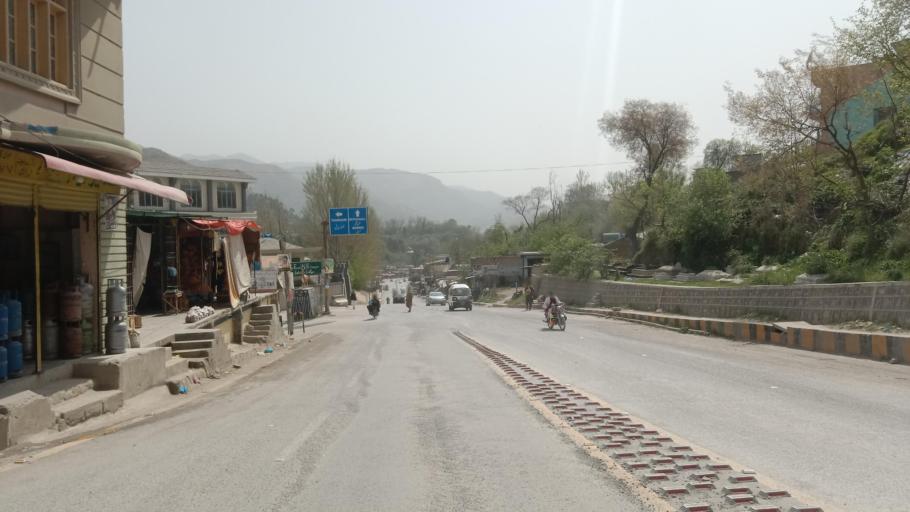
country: PK
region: Khyber Pakhtunkhwa
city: Abbottabad
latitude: 34.1566
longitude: 73.2660
